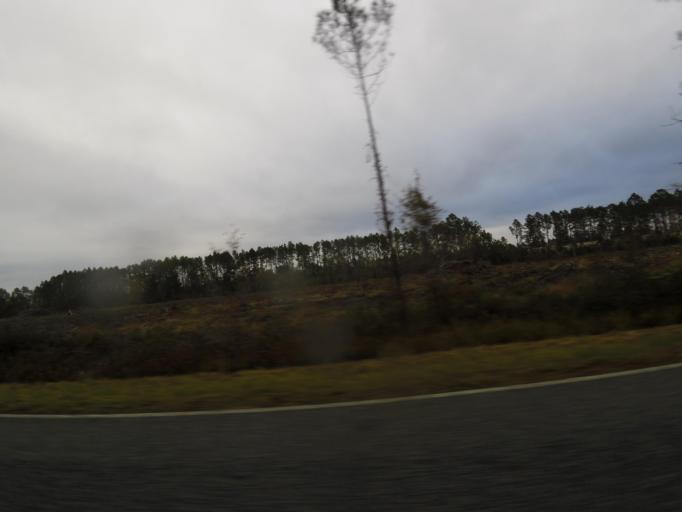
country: US
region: Georgia
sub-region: Charlton County
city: Folkston
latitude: 30.8669
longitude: -82.0398
